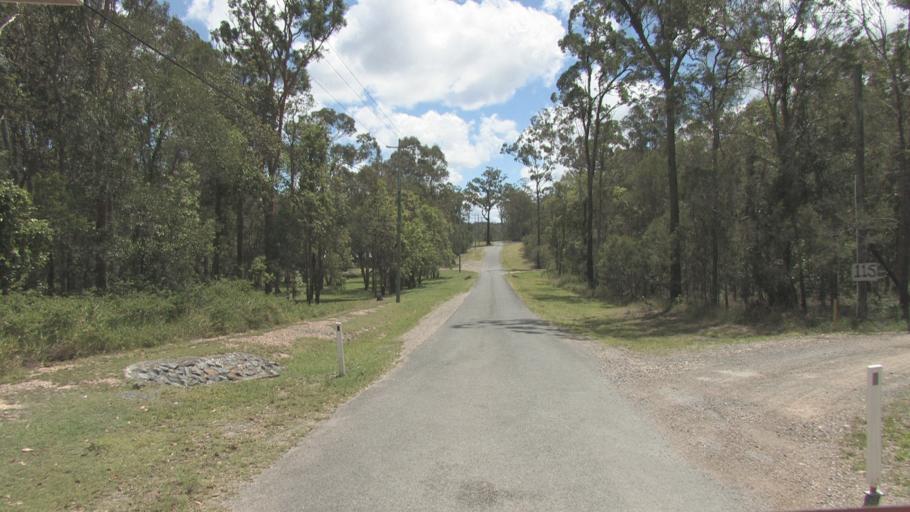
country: AU
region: Queensland
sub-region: Logan
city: Beenleigh
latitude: -27.6476
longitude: 153.2268
